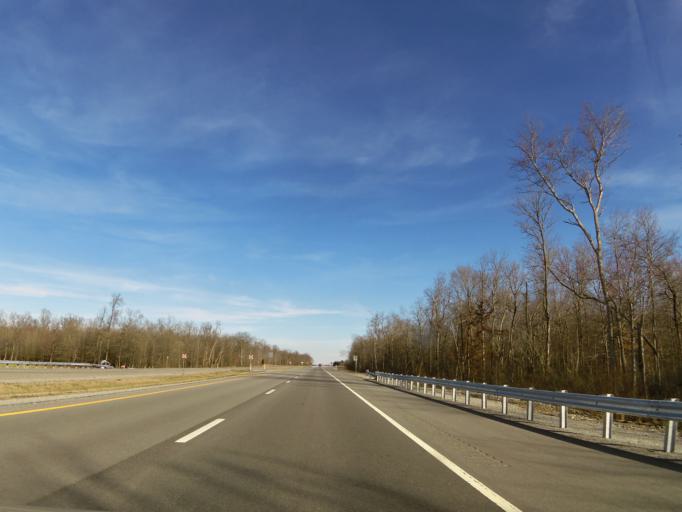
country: US
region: Tennessee
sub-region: Warren County
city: McMinnville
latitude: 35.7177
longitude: -85.8662
